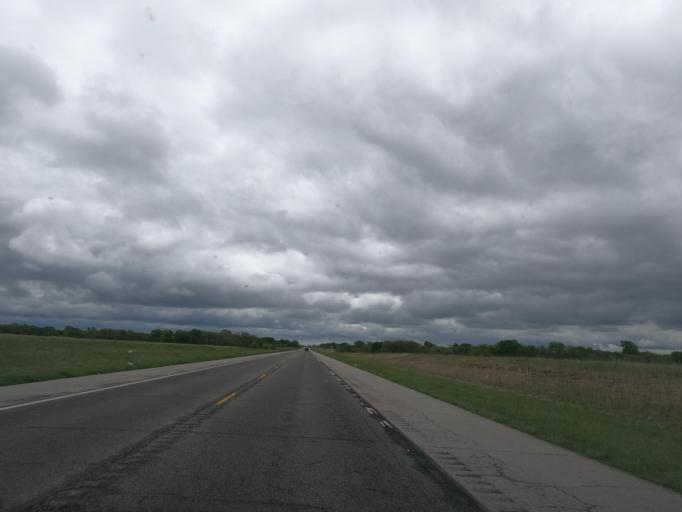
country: US
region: Kansas
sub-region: Labette County
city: Parsons
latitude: 37.3429
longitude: -95.3911
